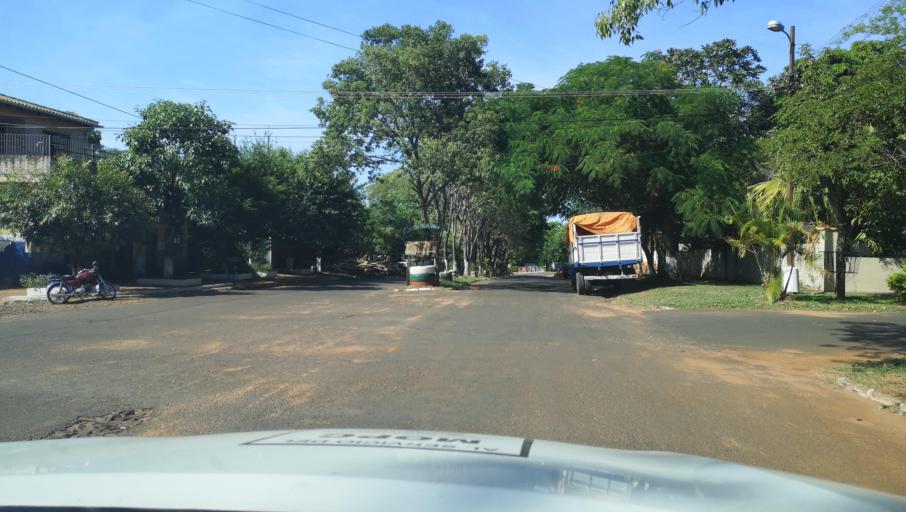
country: PY
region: Misiones
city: Santa Maria
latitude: -26.8931
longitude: -57.0196
